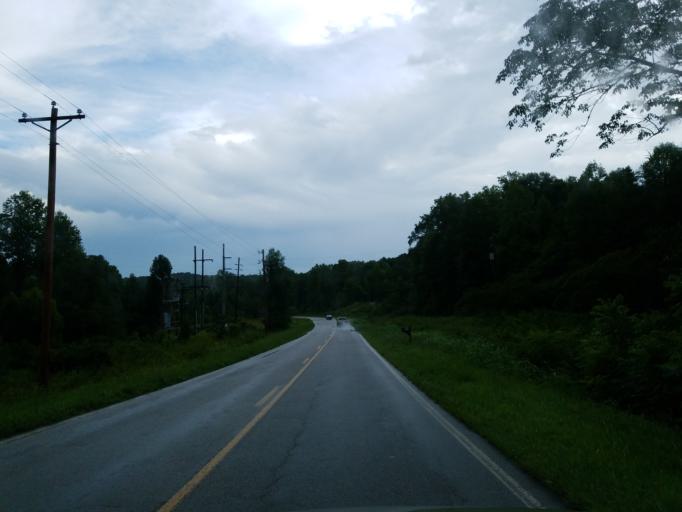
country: US
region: Georgia
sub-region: Lumpkin County
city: Dahlonega
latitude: 34.5238
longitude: -83.9113
